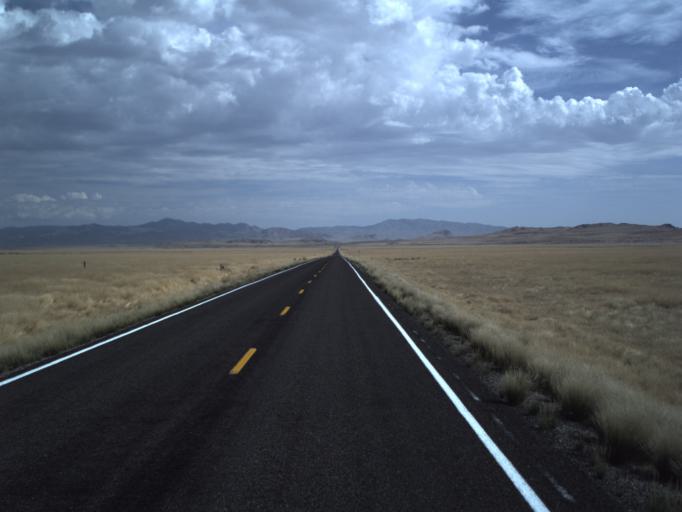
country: US
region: Utah
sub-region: Tooele County
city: Wendover
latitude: 41.3829
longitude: -113.9900
